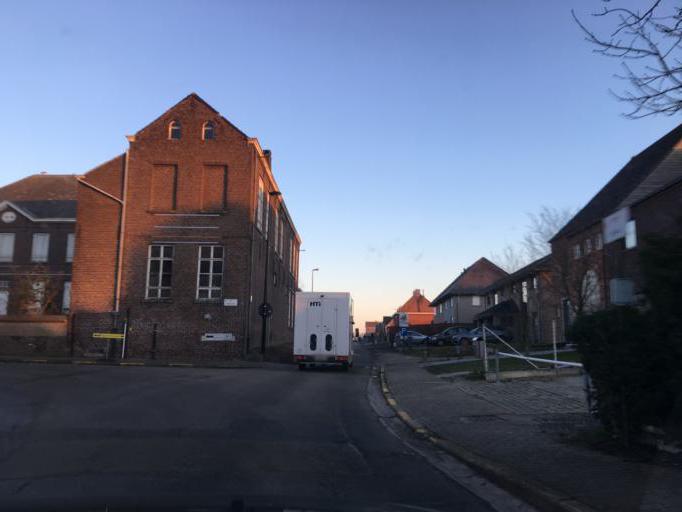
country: BE
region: Flanders
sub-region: Provincie Oost-Vlaanderen
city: Aalter
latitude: 51.1313
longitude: 3.4846
